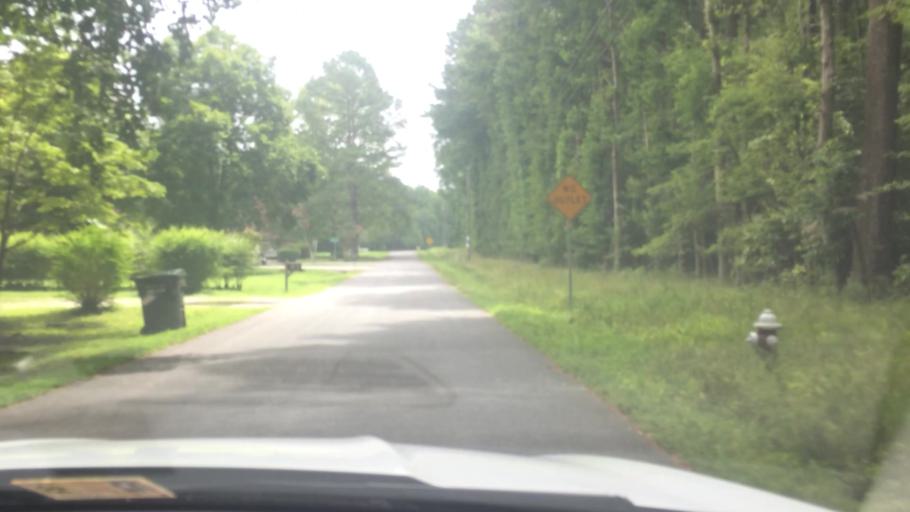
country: US
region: Virginia
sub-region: York County
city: Yorktown
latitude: 37.2196
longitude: -76.5432
